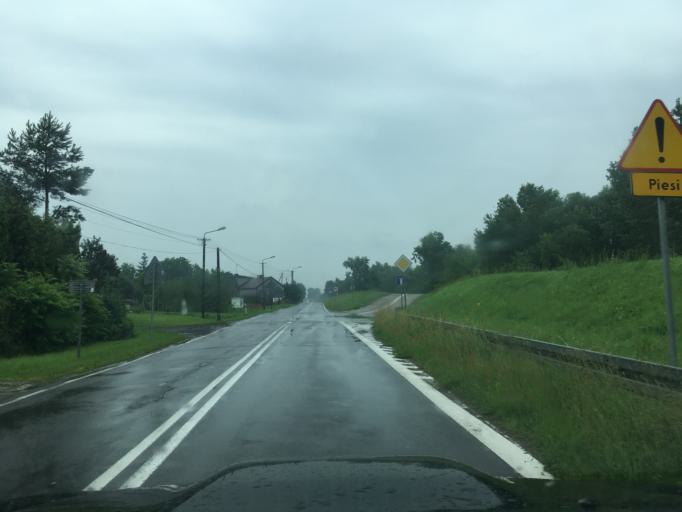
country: PL
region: Masovian Voivodeship
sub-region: Powiat piaseczynski
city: Gora Kalwaria
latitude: 51.9900
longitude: 21.2426
